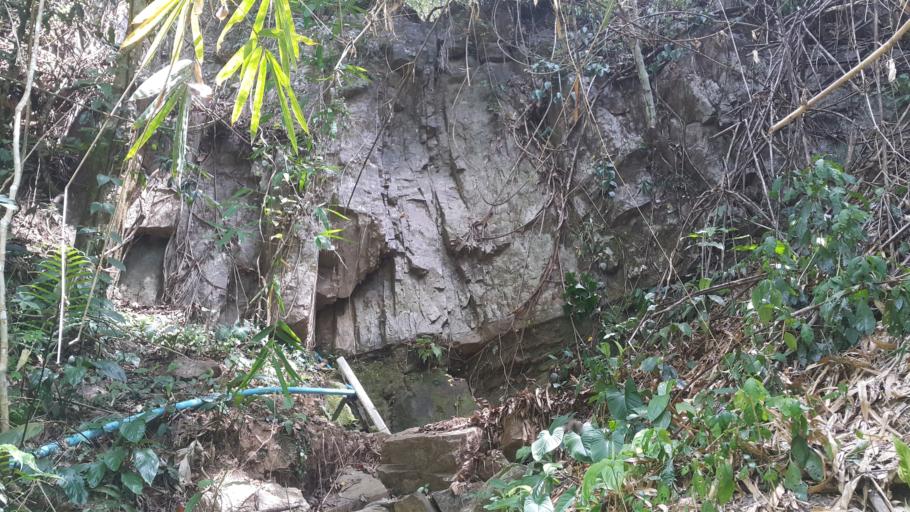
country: TH
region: Lamphun
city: Ban Thi
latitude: 18.6776
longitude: 99.2082
